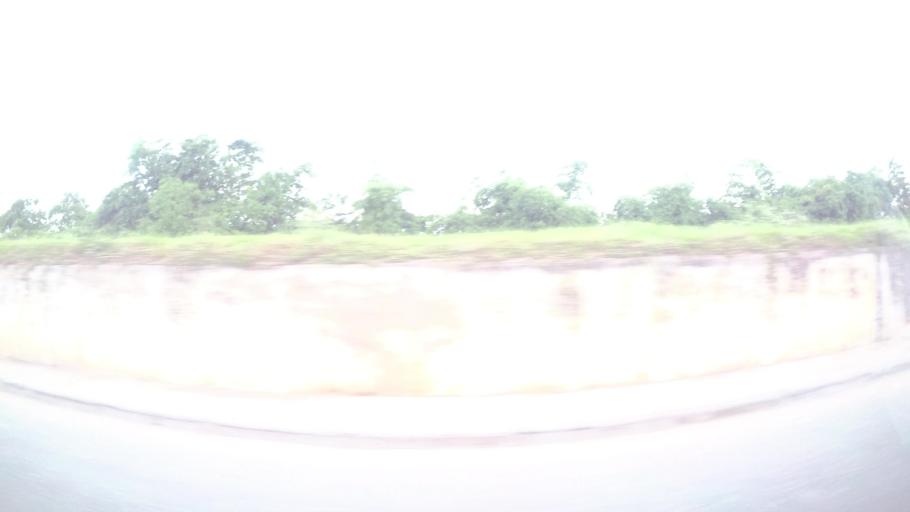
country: VN
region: Ha Noi
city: Trau Quy
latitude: 21.0519
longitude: 105.9242
